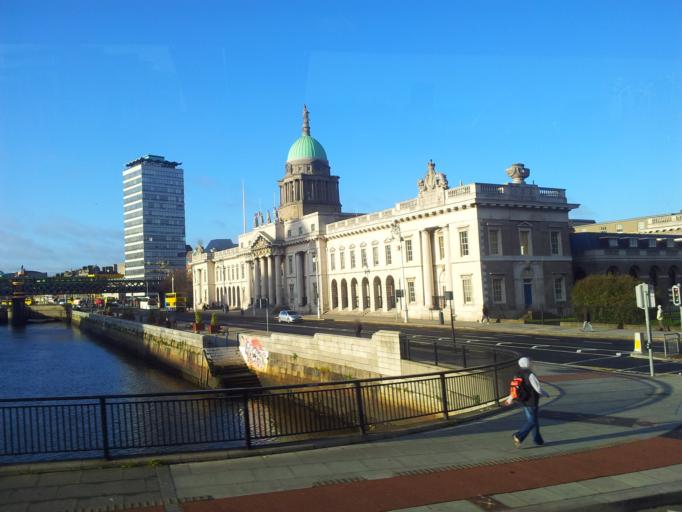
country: IE
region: Leinster
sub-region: Dublin City
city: Dublin
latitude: 53.3482
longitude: -6.2542
